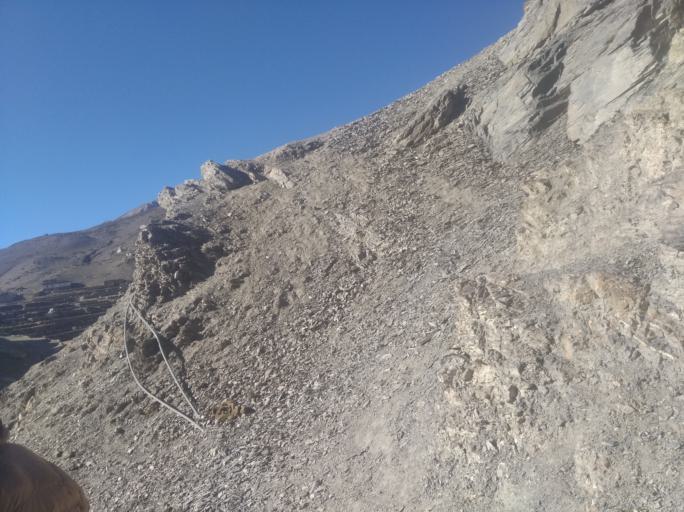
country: NP
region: Western Region
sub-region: Dhawalagiri Zone
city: Jomsom
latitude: 29.0895
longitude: 83.4172
